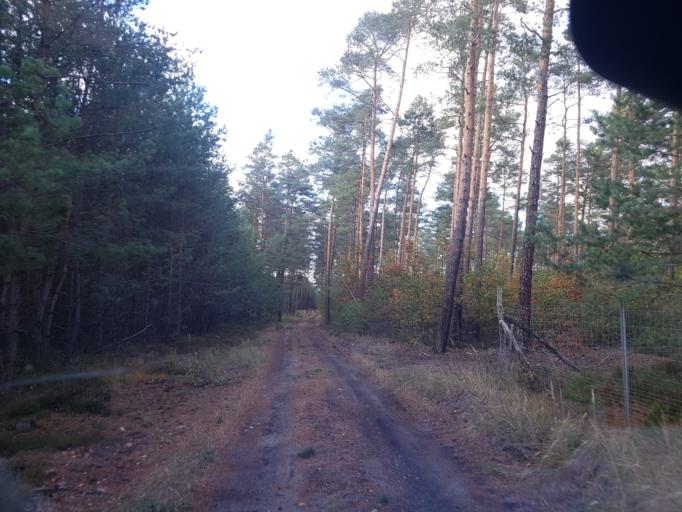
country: DE
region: Brandenburg
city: Finsterwalde
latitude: 51.5547
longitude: 13.6998
